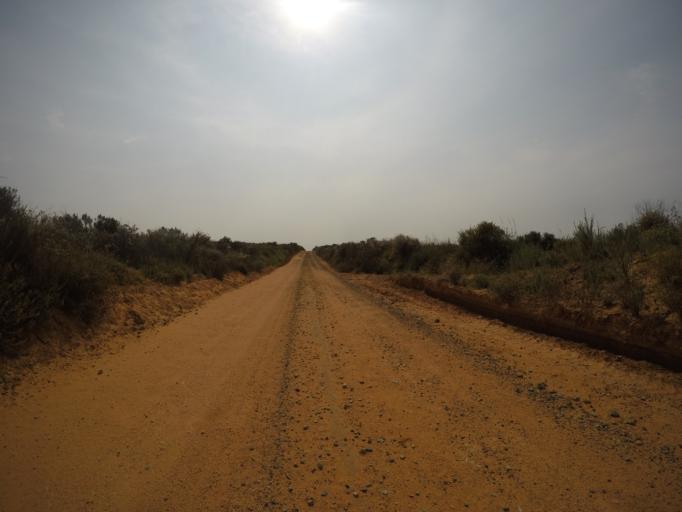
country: ZA
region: Western Cape
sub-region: West Coast District Municipality
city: Malmesbury
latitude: -33.4490
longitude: 18.7462
